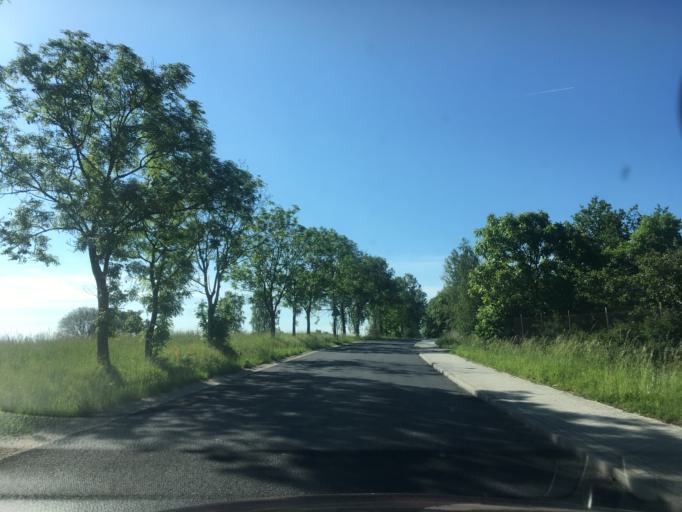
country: PL
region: Lower Silesian Voivodeship
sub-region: Powiat zgorzelecki
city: Zgorzelec
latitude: 51.1255
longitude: 15.0181
